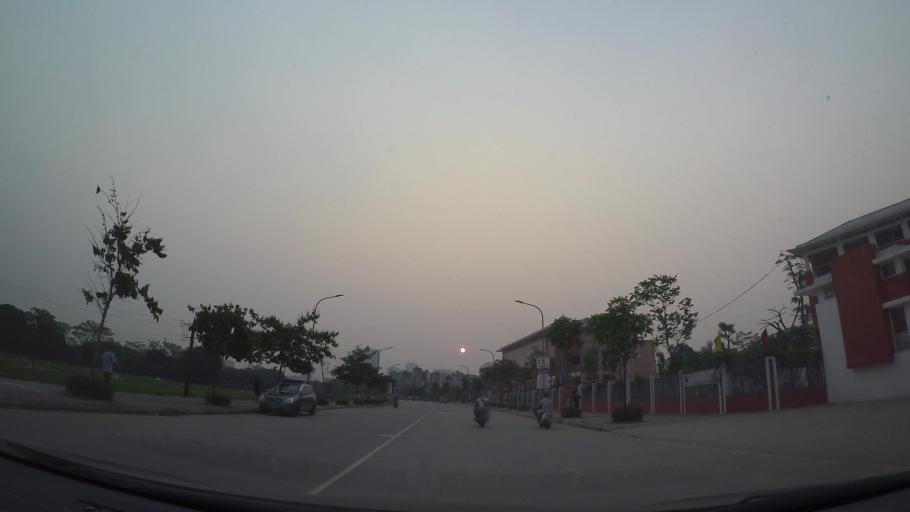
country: VN
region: Ha Noi
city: Thanh Xuan
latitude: 20.9773
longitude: 105.8015
